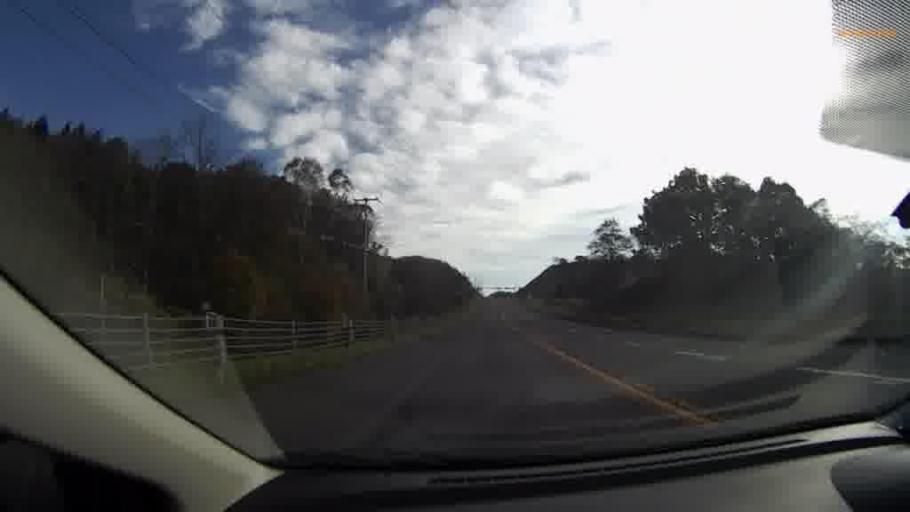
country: JP
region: Hokkaido
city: Kushiro
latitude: 42.9098
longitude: 143.9759
